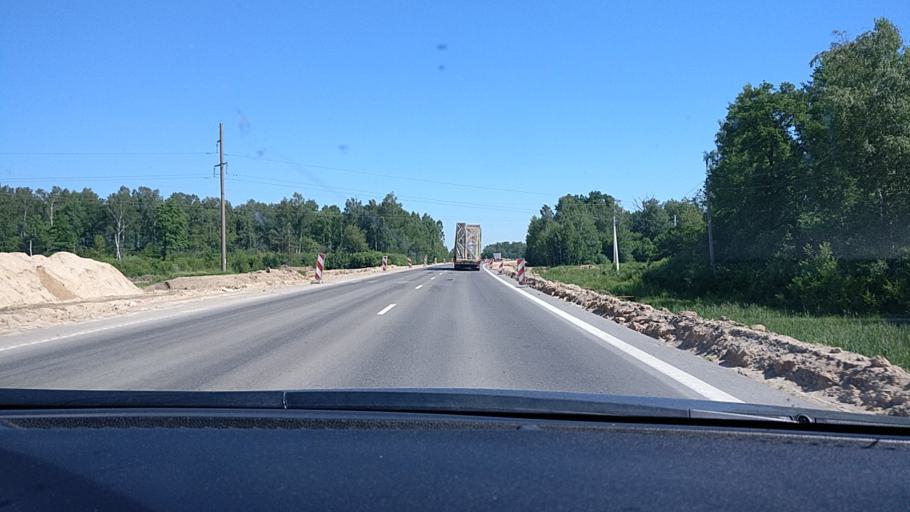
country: LT
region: Panevezys
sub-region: Panevezys City
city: Panevezys
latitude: 55.7568
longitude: 24.2816
